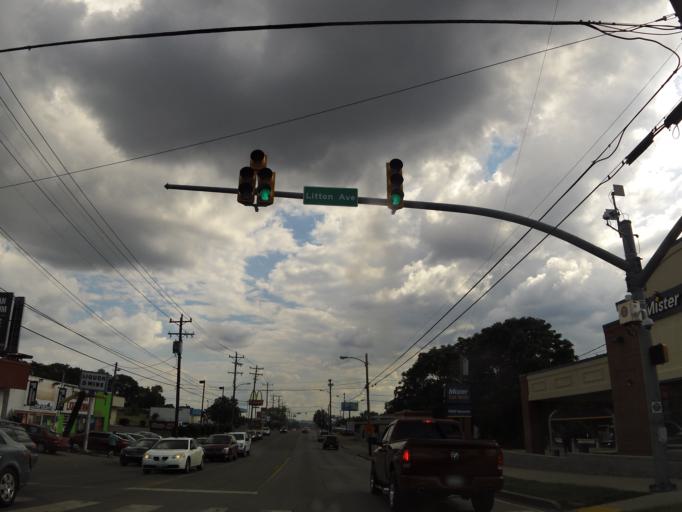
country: US
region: Tennessee
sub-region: Davidson County
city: Nashville
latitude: 36.2025
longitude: -86.7391
